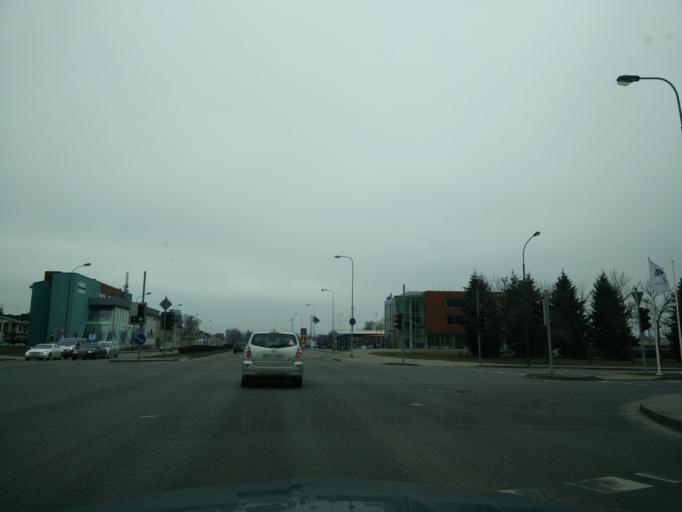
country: LT
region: Klaipedos apskritis
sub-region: Klaipeda
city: Klaipeda
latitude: 55.6895
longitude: 21.1444
